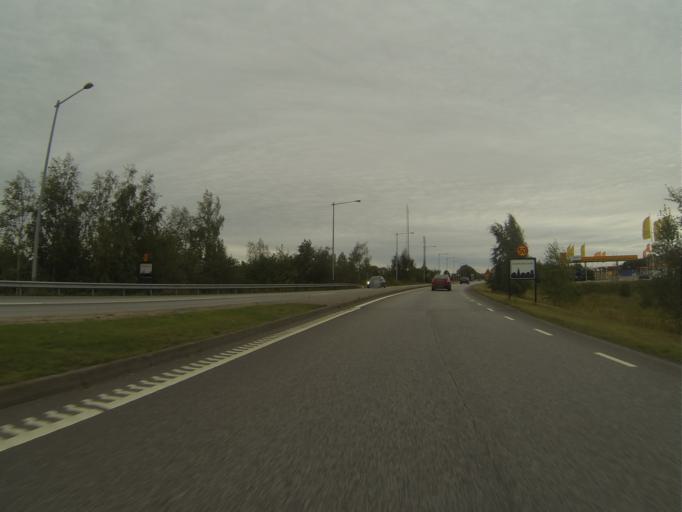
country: SE
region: Skane
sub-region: Staffanstorps Kommun
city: Staffanstorp
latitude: 55.6284
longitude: 13.1859
